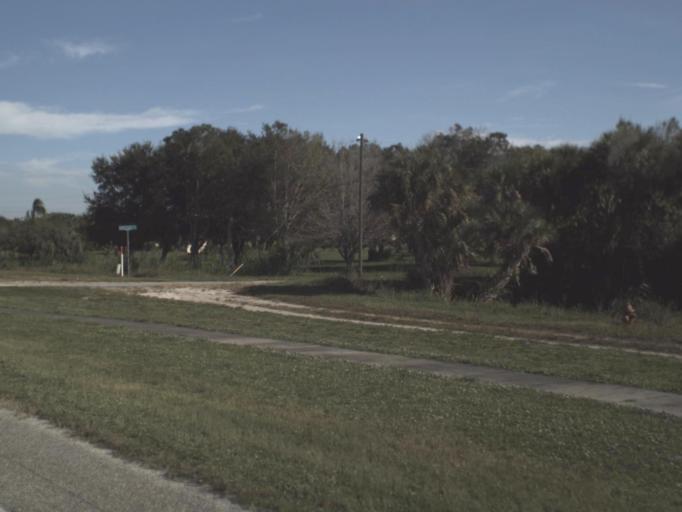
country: US
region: Florida
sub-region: Glades County
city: Moore Haven
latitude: 26.8337
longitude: -81.1122
